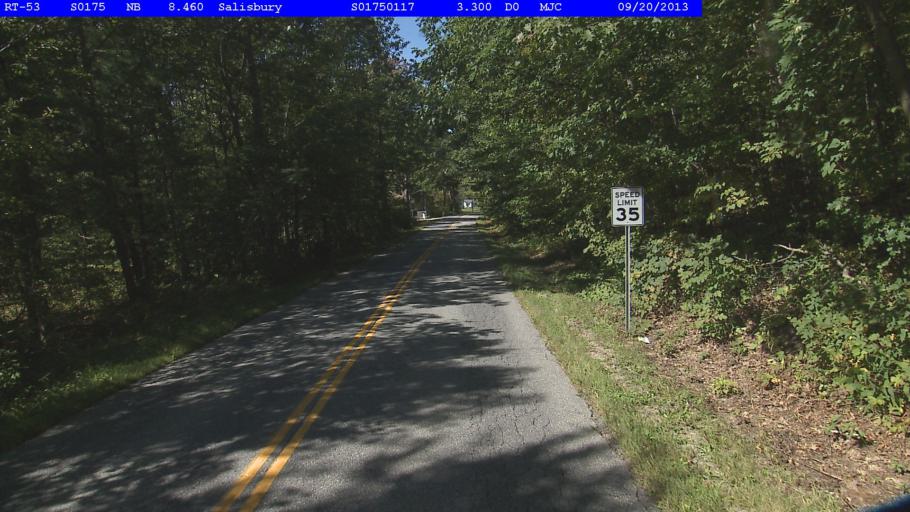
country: US
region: Vermont
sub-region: Addison County
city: Middlebury (village)
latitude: 43.9242
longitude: -73.0951
